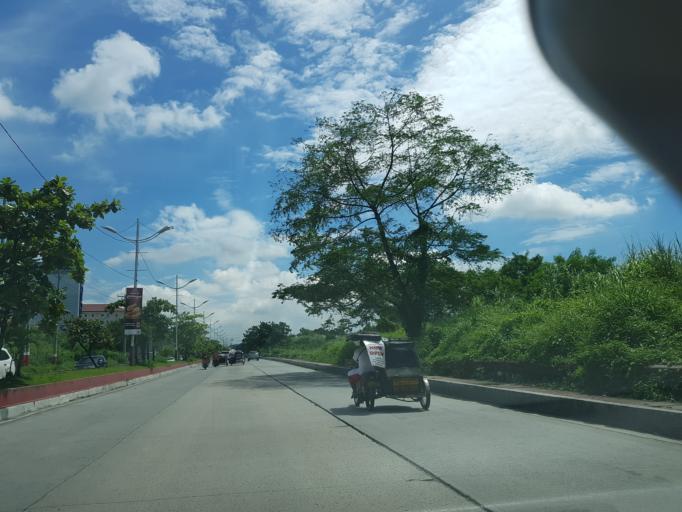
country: PH
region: Calabarzon
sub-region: Province of Rizal
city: Pateros
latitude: 14.5291
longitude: 121.0637
